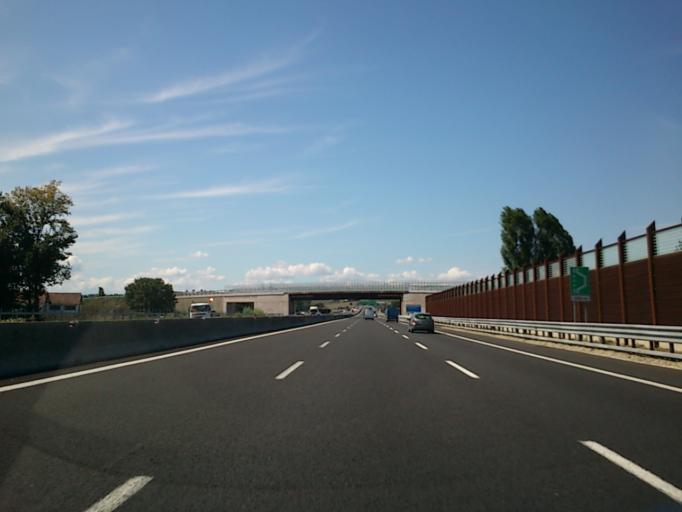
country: IT
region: The Marches
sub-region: Provincia di Pesaro e Urbino
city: Villa Ceccolini
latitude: 43.8993
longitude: 12.8551
